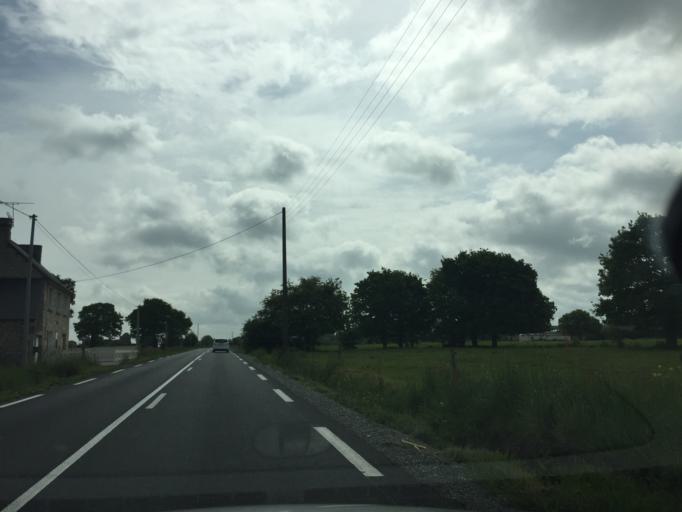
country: FR
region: Brittany
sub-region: Departement des Cotes-d'Armor
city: Crehen
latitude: 48.5664
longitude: -2.2010
